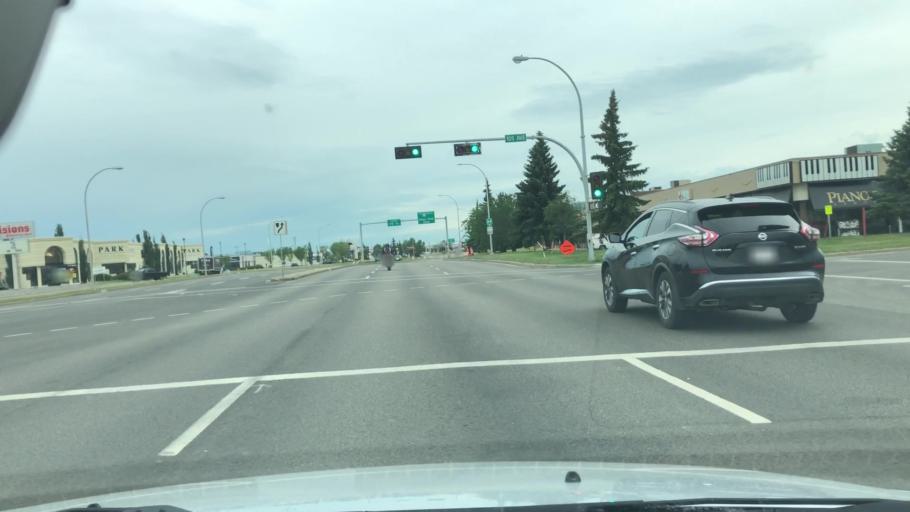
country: CA
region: Alberta
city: St. Albert
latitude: 53.5488
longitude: -113.6154
